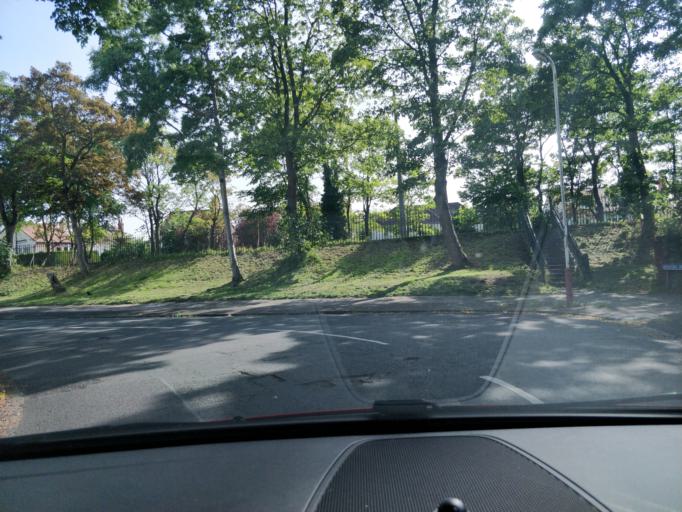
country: GB
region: England
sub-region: Sefton
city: Southport
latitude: 53.6571
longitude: -2.9751
